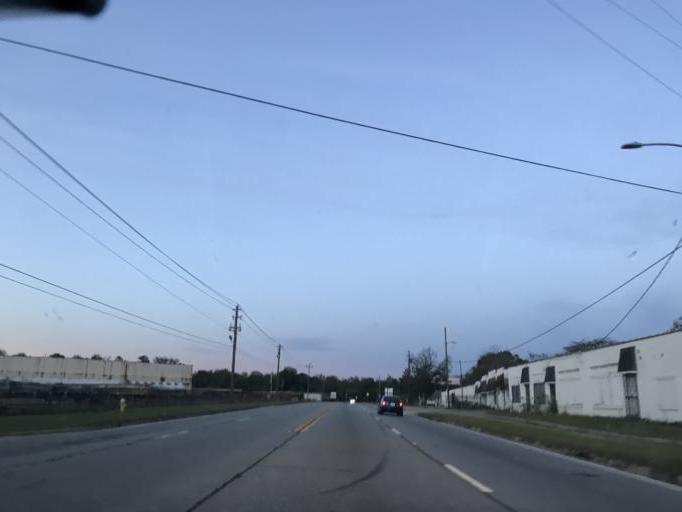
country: US
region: Georgia
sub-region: Bibb County
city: Macon
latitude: 32.7888
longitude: -83.6517
